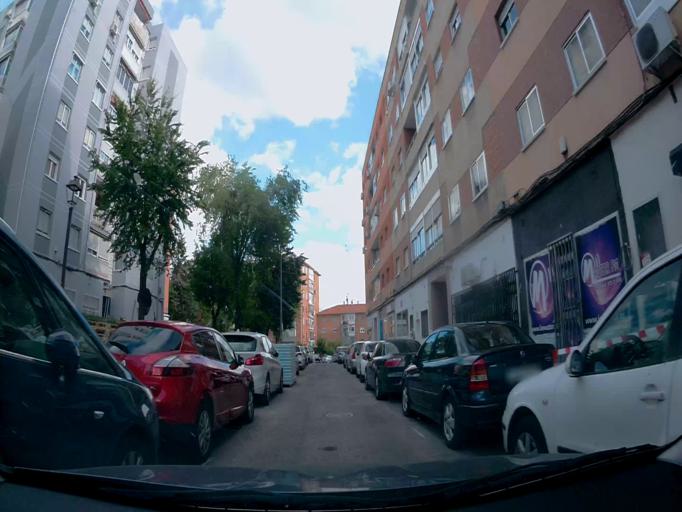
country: ES
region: Madrid
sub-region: Provincia de Madrid
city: Mostoles
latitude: 40.3210
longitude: -3.8735
